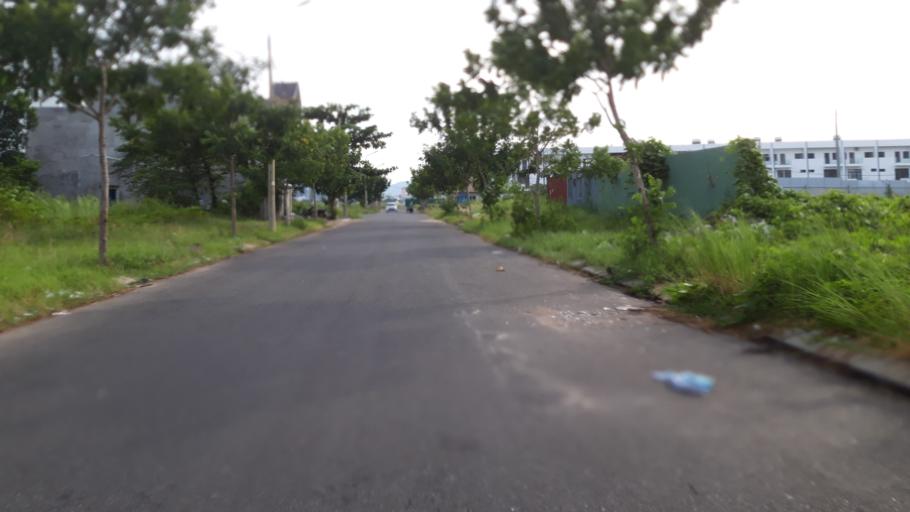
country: VN
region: Da Nang
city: Da Nang
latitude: 16.0918
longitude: 108.2279
